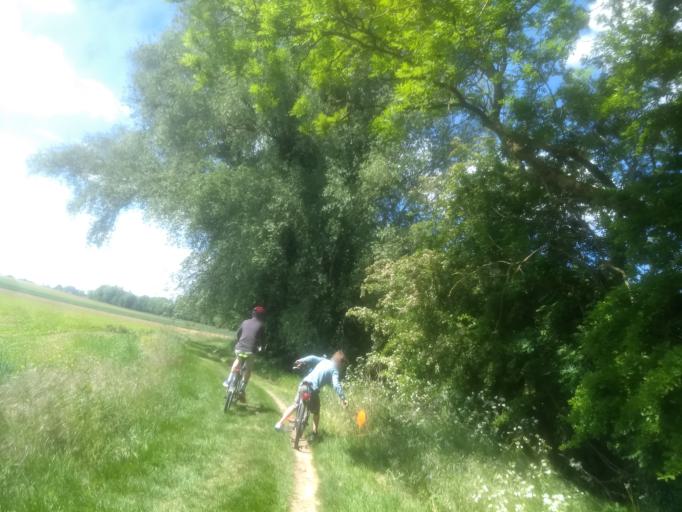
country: FR
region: Nord-Pas-de-Calais
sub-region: Departement du Pas-de-Calais
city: Agny
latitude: 50.2549
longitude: 2.7416
